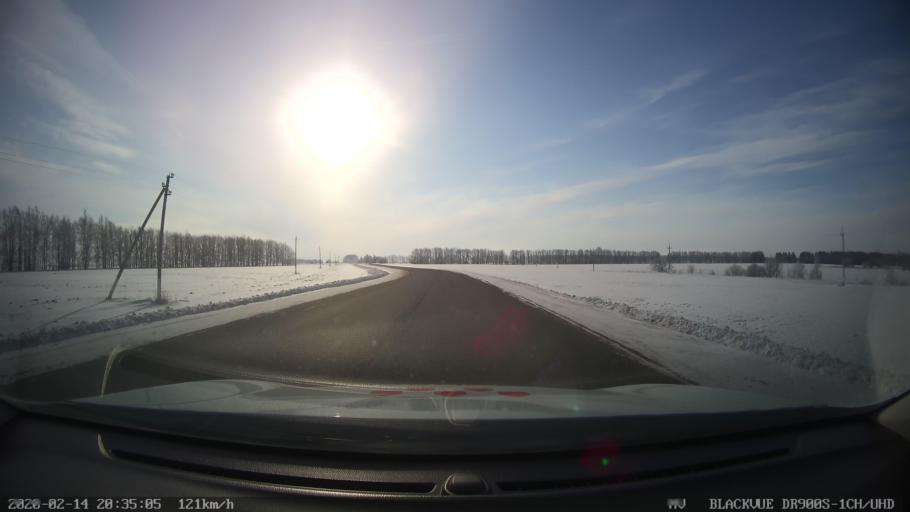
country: RU
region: Tatarstan
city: Kuybyshevskiy Zaton
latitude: 55.3877
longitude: 48.9801
